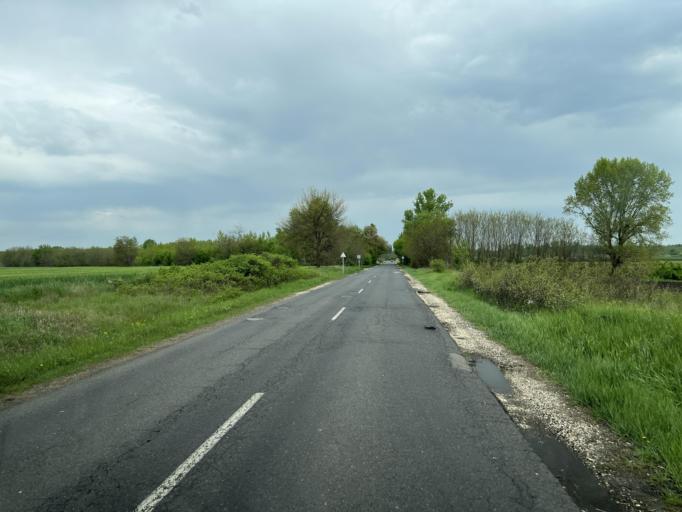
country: HU
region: Pest
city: Farmos
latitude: 47.3925
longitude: 19.8923
